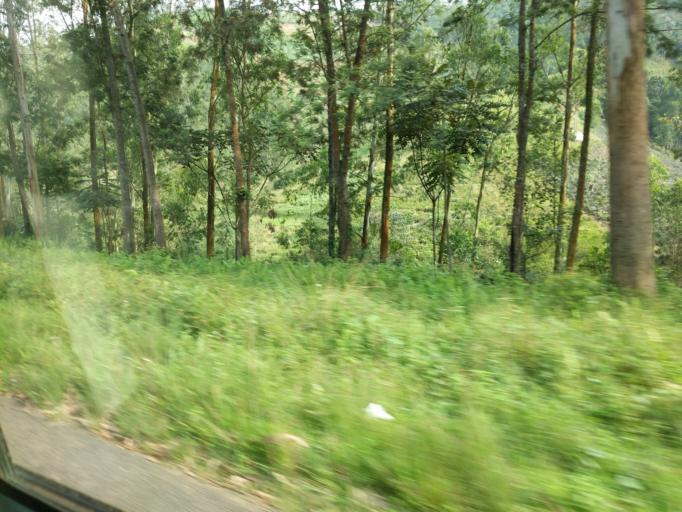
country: RW
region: Northern Province
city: Musanze
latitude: -1.6576
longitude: 29.8130
